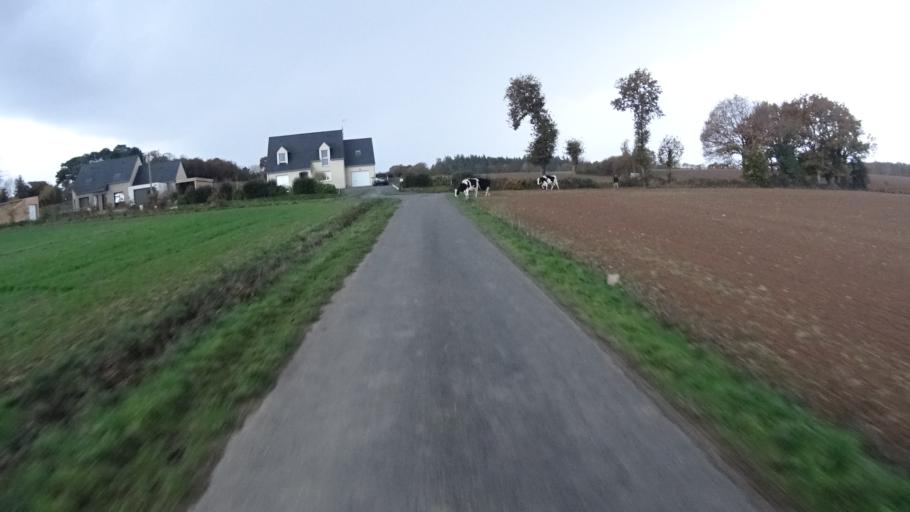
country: FR
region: Pays de la Loire
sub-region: Departement de la Loire-Atlantique
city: Avessac
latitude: 47.6591
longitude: -1.9936
